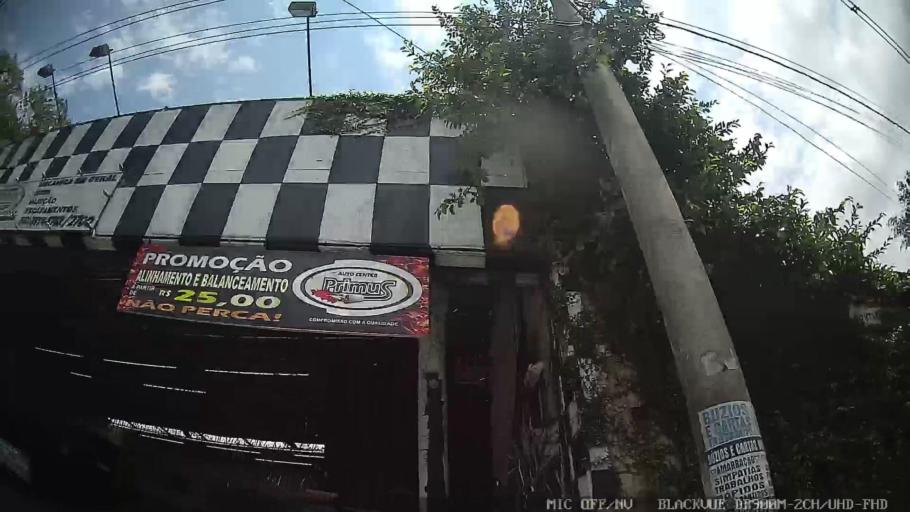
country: BR
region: Sao Paulo
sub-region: Caieiras
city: Caieiras
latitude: -23.4361
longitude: -46.7206
